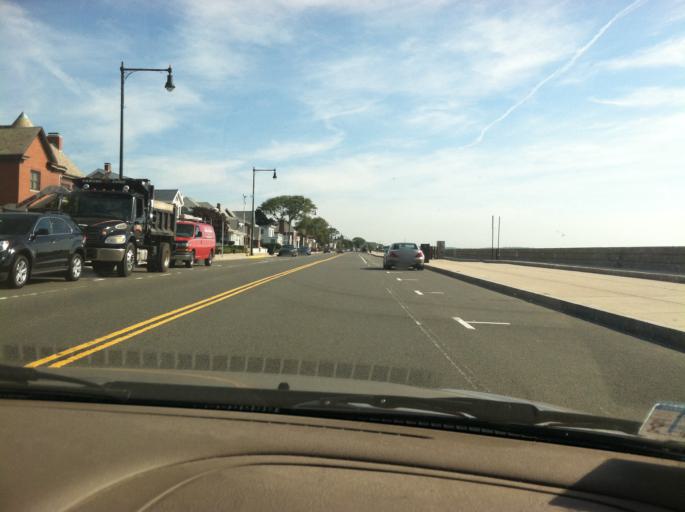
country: US
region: Massachusetts
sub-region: Suffolk County
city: Revere
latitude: 42.4295
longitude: -70.9785
